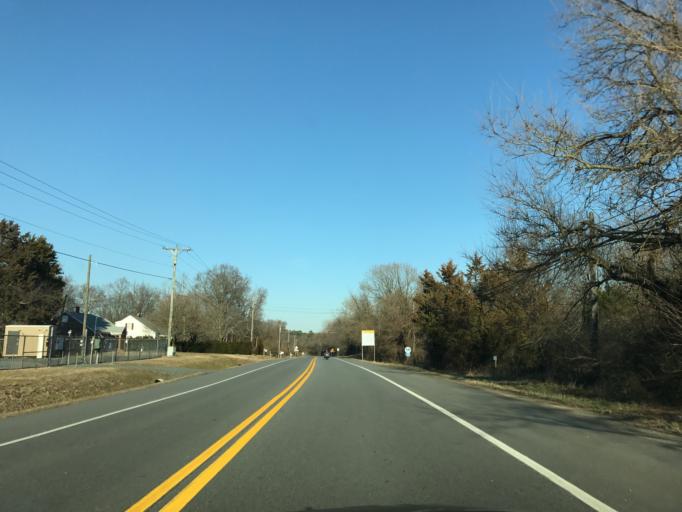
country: US
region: Maryland
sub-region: Queen Anne's County
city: Kingstown
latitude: 39.2519
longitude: -75.8473
